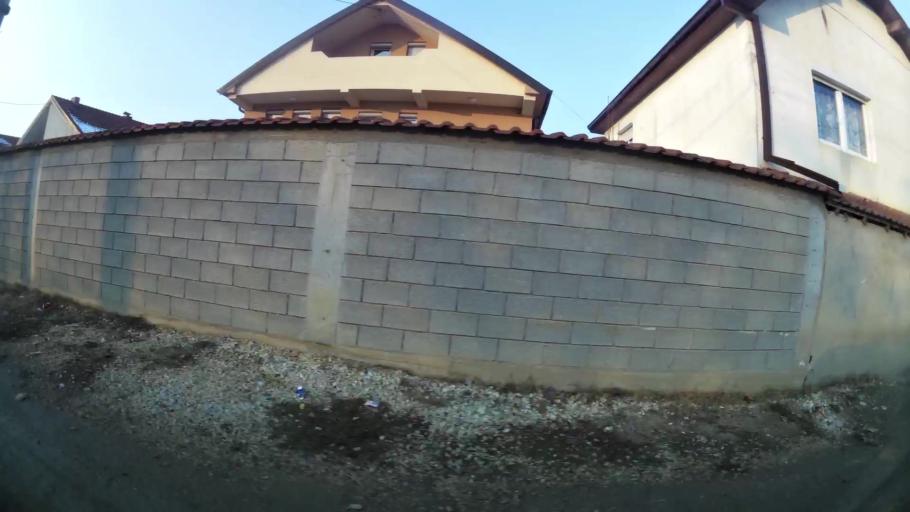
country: MK
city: Creshevo
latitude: 42.0147
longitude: 21.5178
